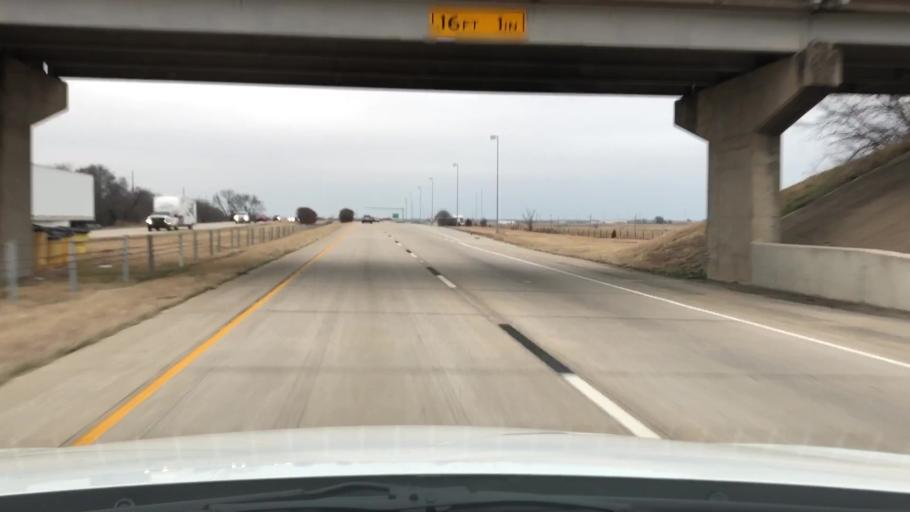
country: US
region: Oklahoma
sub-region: Love County
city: Marietta
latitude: 33.8968
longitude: -97.1343
